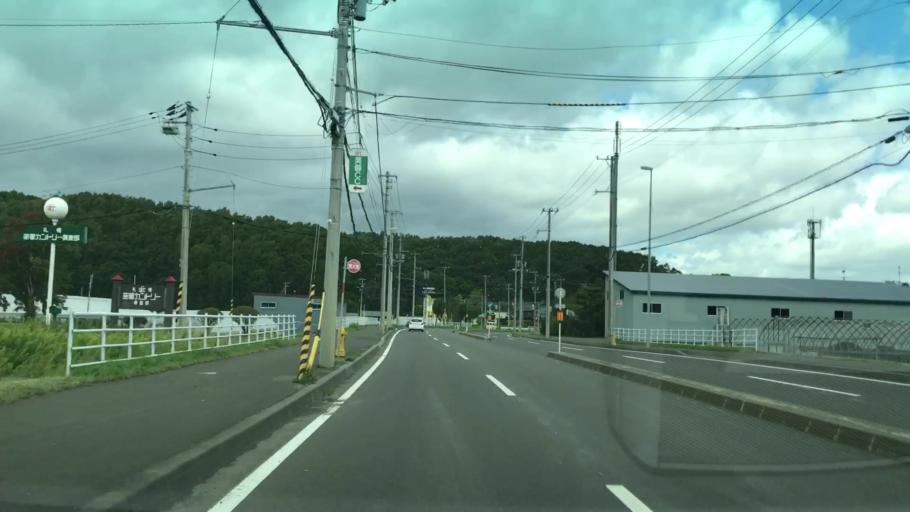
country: JP
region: Hokkaido
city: Kitahiroshima
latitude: 42.9784
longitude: 141.4418
